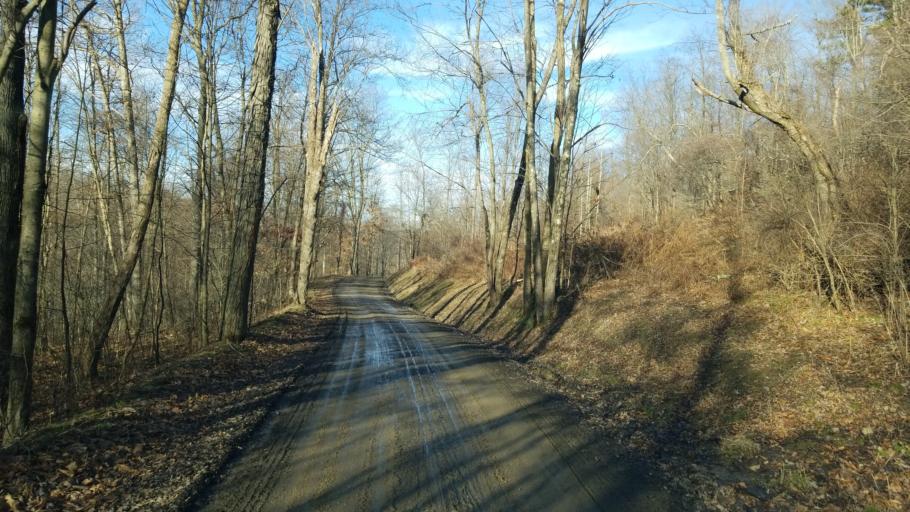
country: US
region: Pennsylvania
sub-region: Indiana County
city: Chevy Chase Heights
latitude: 40.8351
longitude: -79.1739
